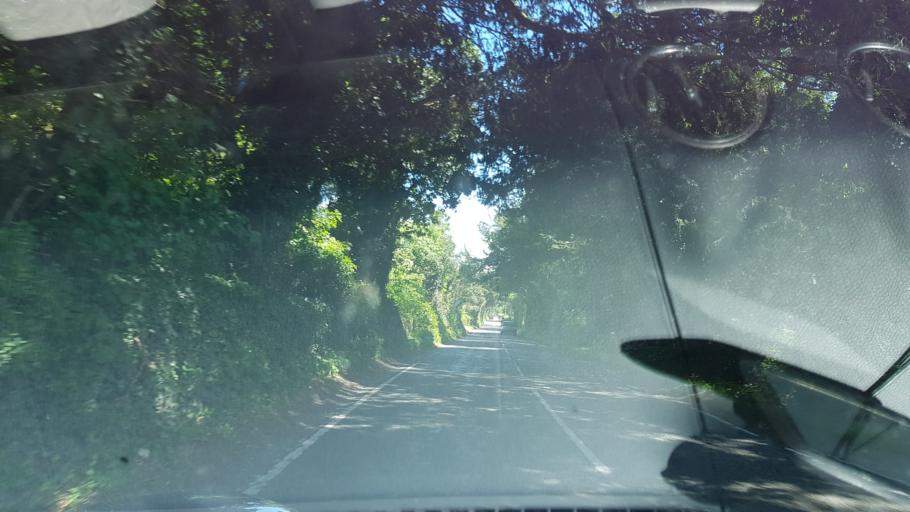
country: GB
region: England
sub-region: Surrey
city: Chiddingfold
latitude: 51.1332
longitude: -0.5647
